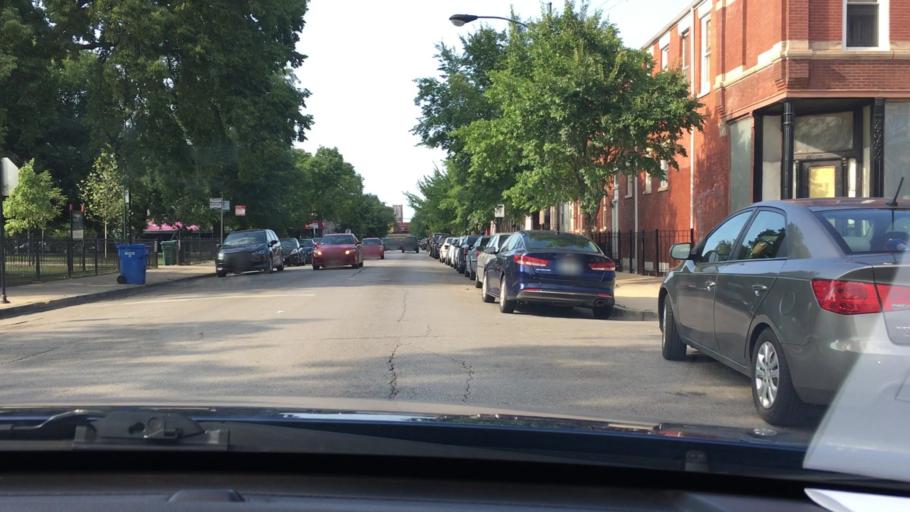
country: US
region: Illinois
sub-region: Cook County
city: Chicago
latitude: 41.8568
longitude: -87.6710
